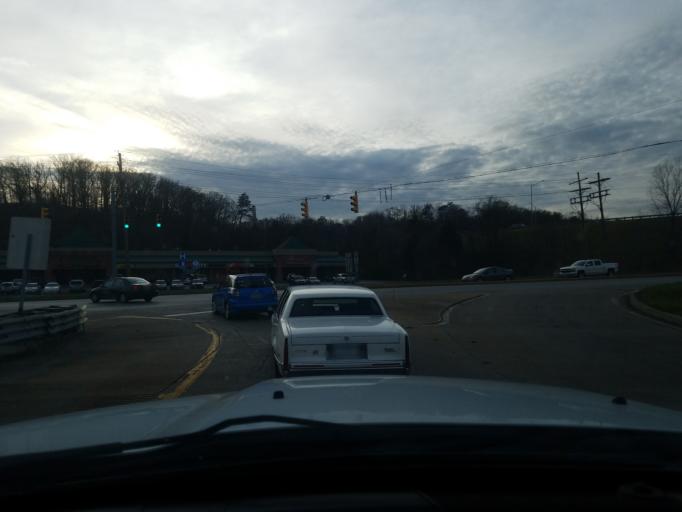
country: US
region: Indiana
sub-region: Floyd County
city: New Albany
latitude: 38.3101
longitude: -85.8444
